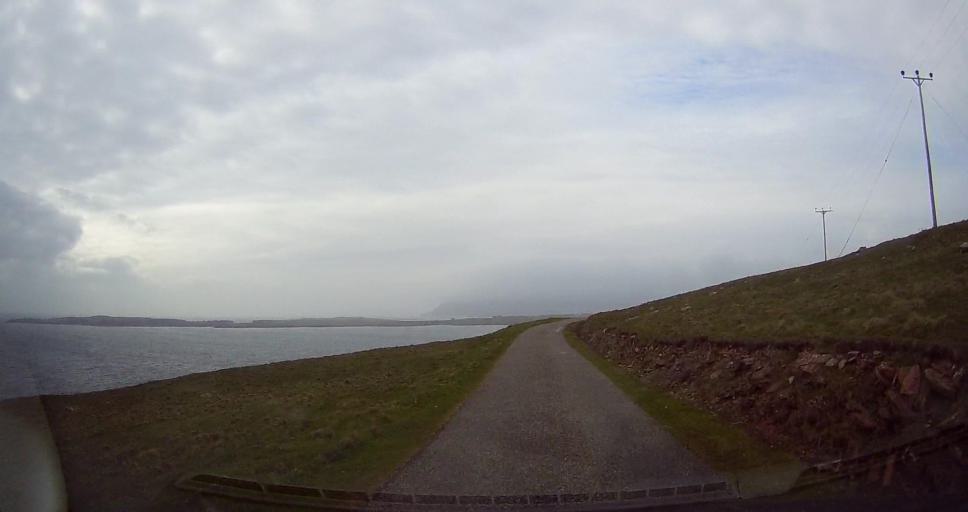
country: GB
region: Scotland
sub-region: Shetland Islands
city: Sandwick
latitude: 59.8592
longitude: -1.2764
